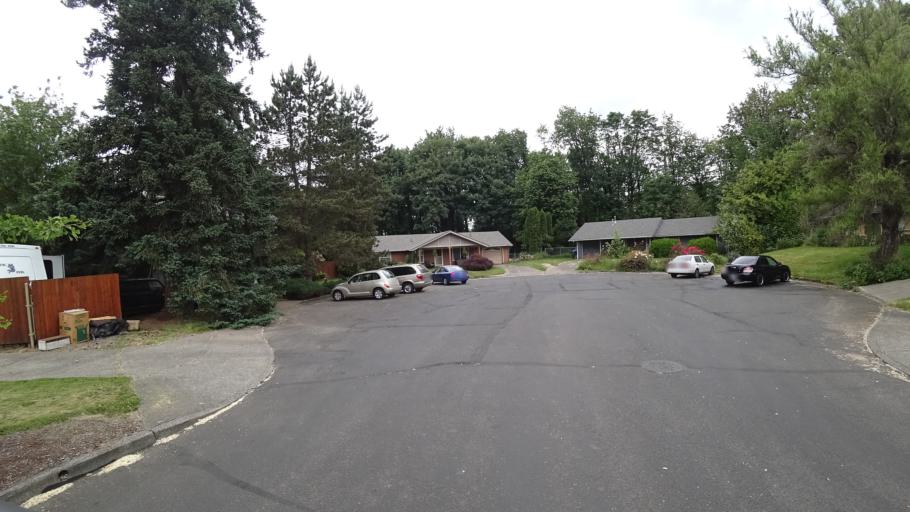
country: US
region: Oregon
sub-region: Multnomah County
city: Lents
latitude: 45.4680
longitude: -122.5588
